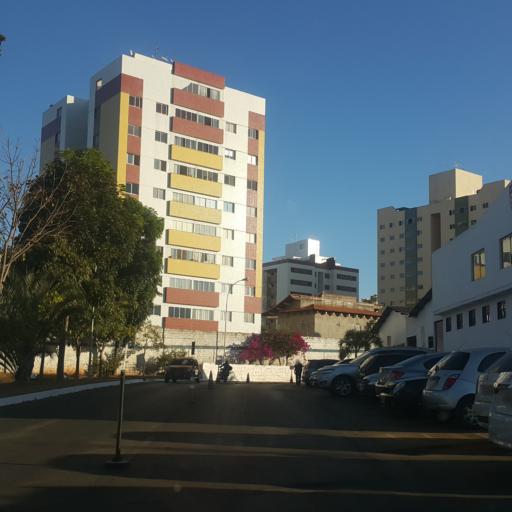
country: BR
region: Federal District
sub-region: Brasilia
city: Brasilia
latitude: -15.8272
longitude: -48.0129
